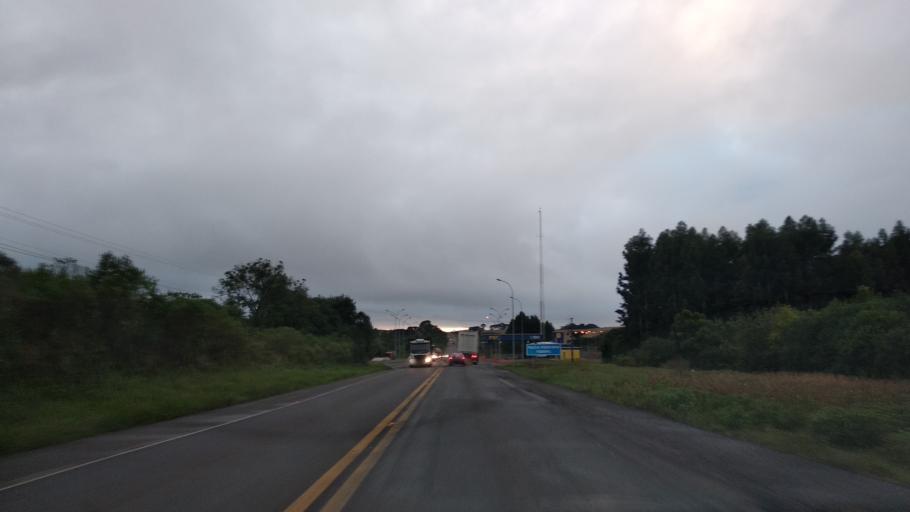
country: BR
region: Santa Catarina
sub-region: Campos Novos
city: Campos Novos
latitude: -27.3880
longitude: -51.1160
